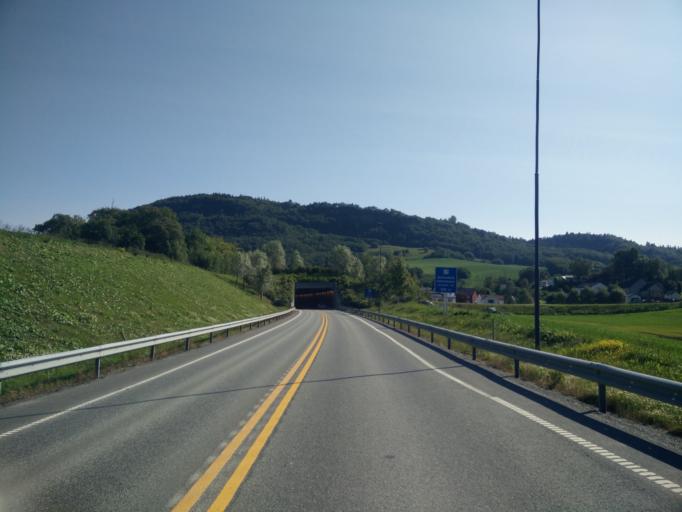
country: NO
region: Sor-Trondelag
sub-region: Melhus
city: Melhus
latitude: 63.3079
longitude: 10.1837
